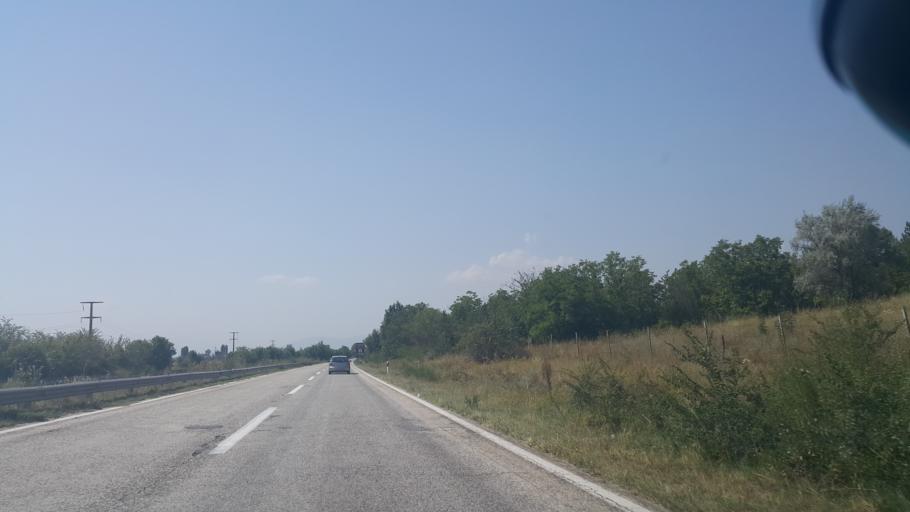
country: MK
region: Petrovec
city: Petrovec
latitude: 41.9116
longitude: 21.6459
